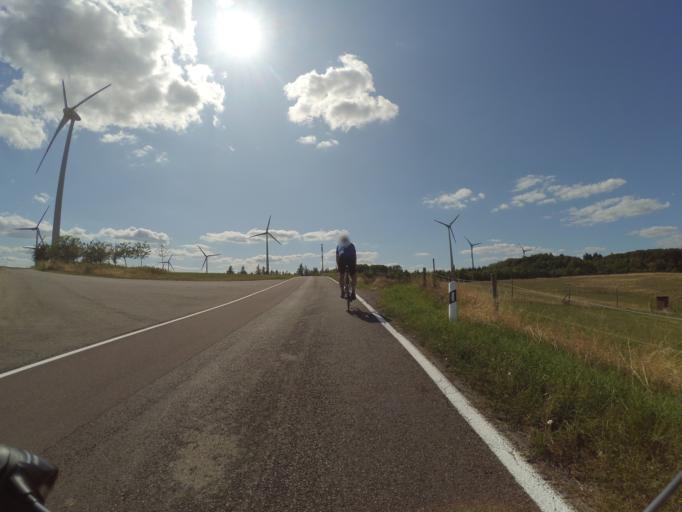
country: DE
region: Rheinland-Pfalz
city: Bescheid
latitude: 49.7560
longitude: 6.8725
